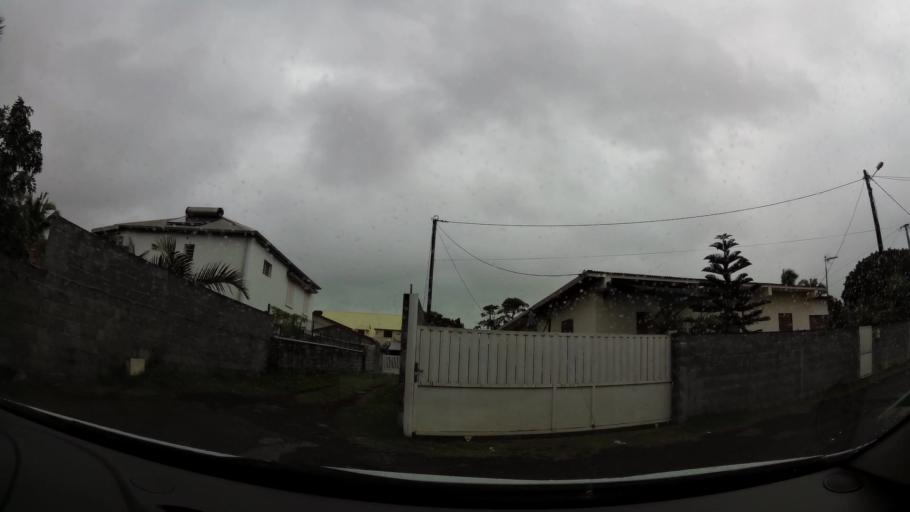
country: RE
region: Reunion
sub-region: Reunion
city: Saint-Andre
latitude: -20.9574
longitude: 55.6532
